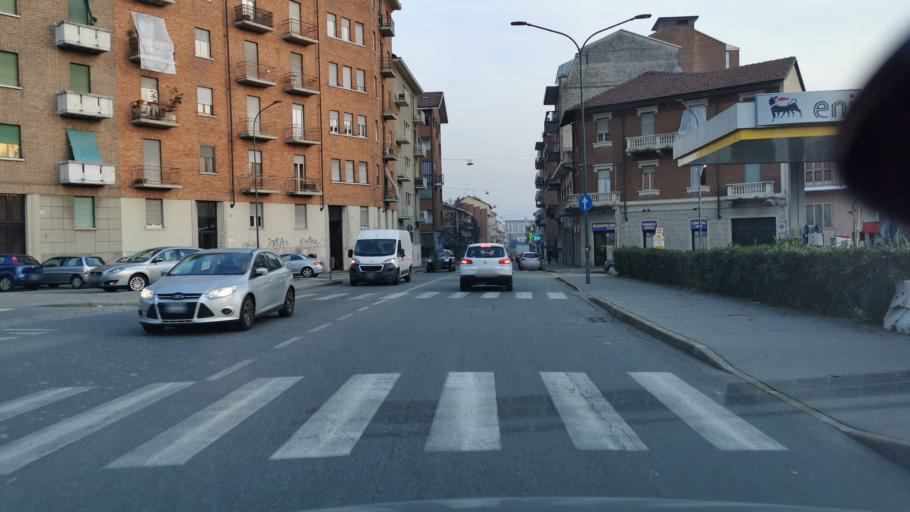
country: IT
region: Piedmont
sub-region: Provincia di Torino
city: Venaria Reale
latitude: 45.0942
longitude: 7.6508
